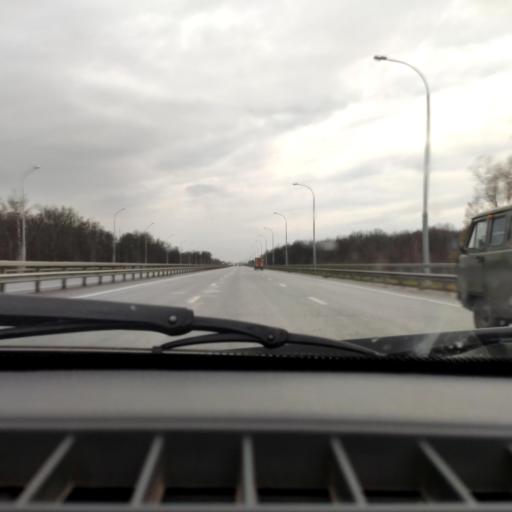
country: RU
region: Bashkortostan
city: Ufa
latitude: 54.6481
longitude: 56.0409
